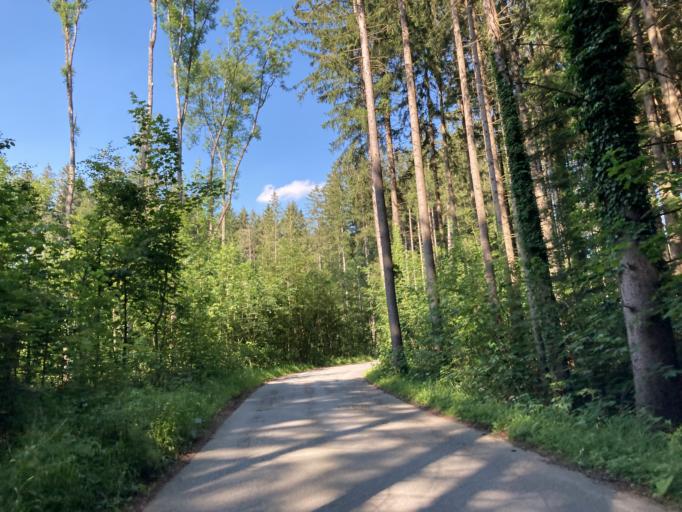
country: DE
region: Bavaria
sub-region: Upper Bavaria
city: Samerberg
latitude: 47.7530
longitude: 12.2015
